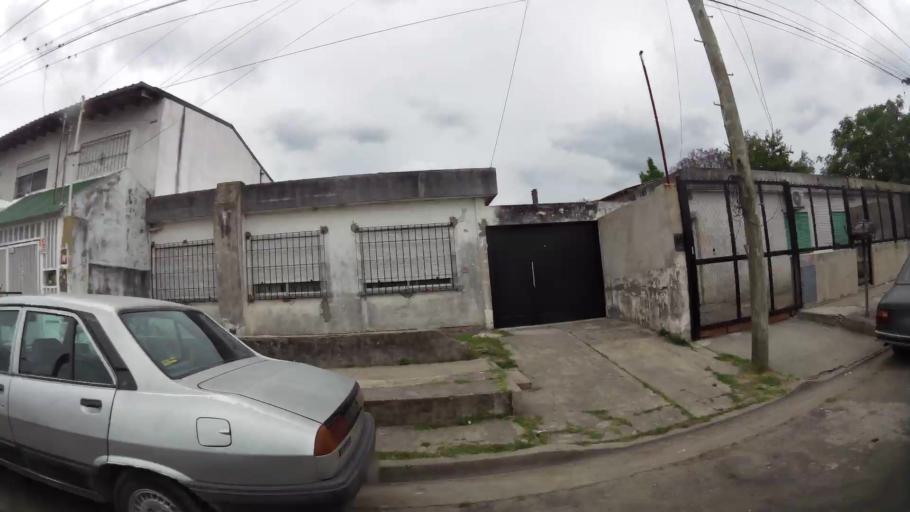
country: AR
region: Buenos Aires
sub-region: Partido de Zarate
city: Zarate
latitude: -34.1150
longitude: -59.0181
